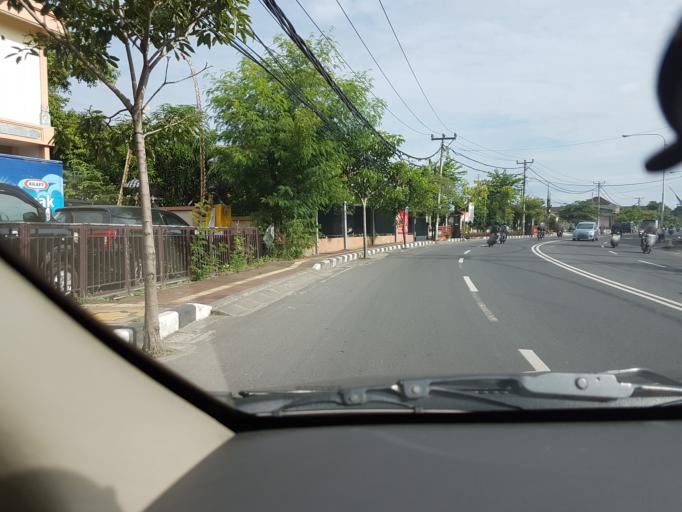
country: ID
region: Bali
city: Denpasar
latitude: -8.6742
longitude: 115.1897
